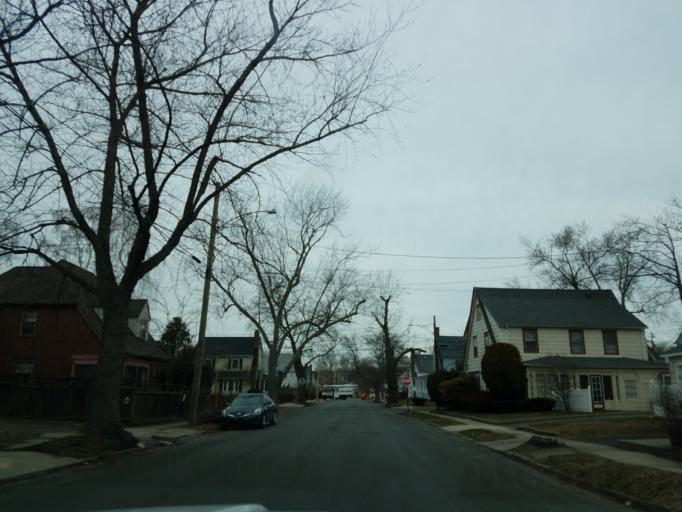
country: US
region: Connecticut
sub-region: Fairfield County
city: Bridgeport
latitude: 41.1861
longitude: -73.2122
